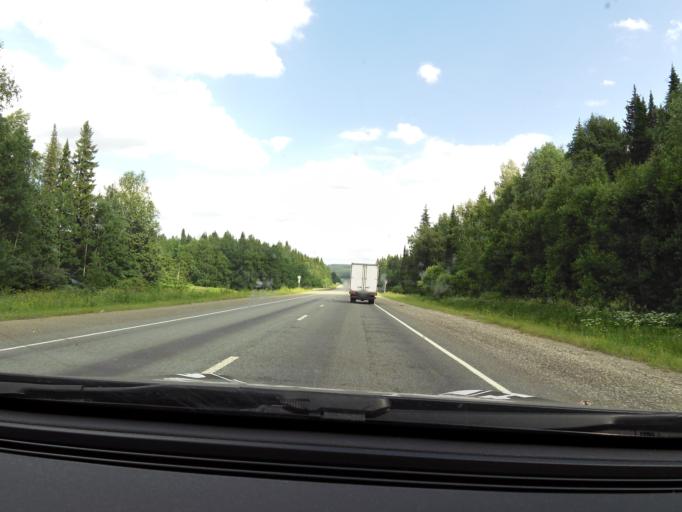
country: RU
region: Sverdlovsk
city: Bisert'
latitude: 56.8285
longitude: 59.1398
